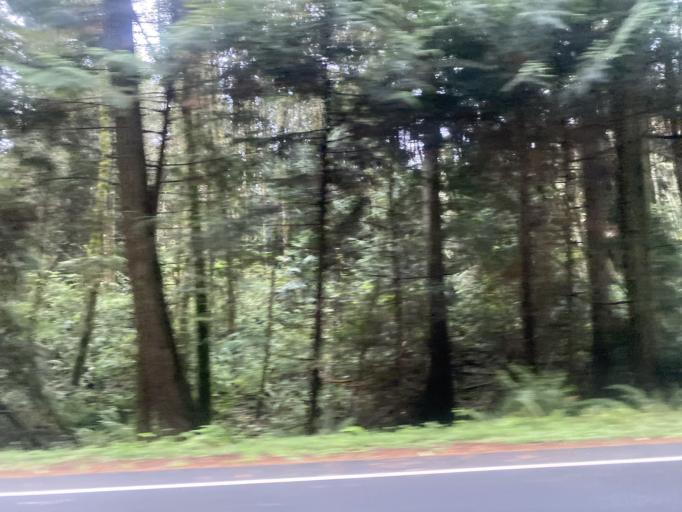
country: US
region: Washington
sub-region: Island County
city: Freeland
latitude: 48.0736
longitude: -122.4850
